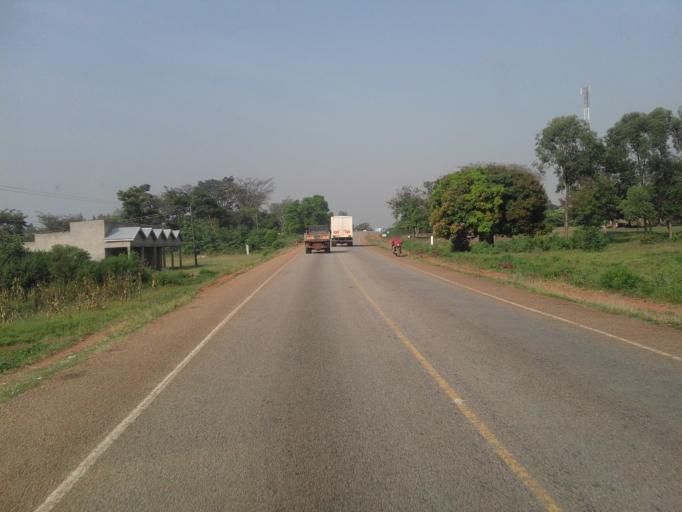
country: UG
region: Eastern Region
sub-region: Budaka District
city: Budaka
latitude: 1.0397
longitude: 34.0216
